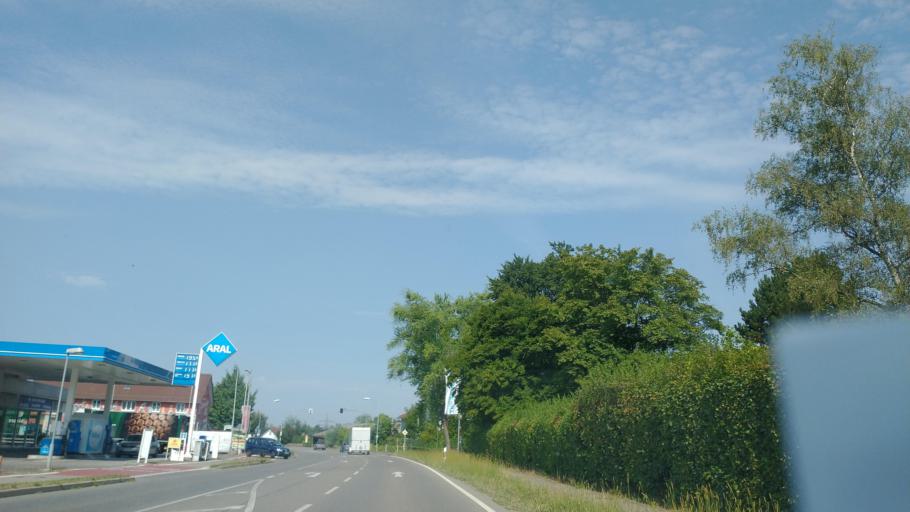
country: DE
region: Baden-Wuerttemberg
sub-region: Tuebingen Region
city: Tettnang
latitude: 47.6684
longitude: 9.5618
